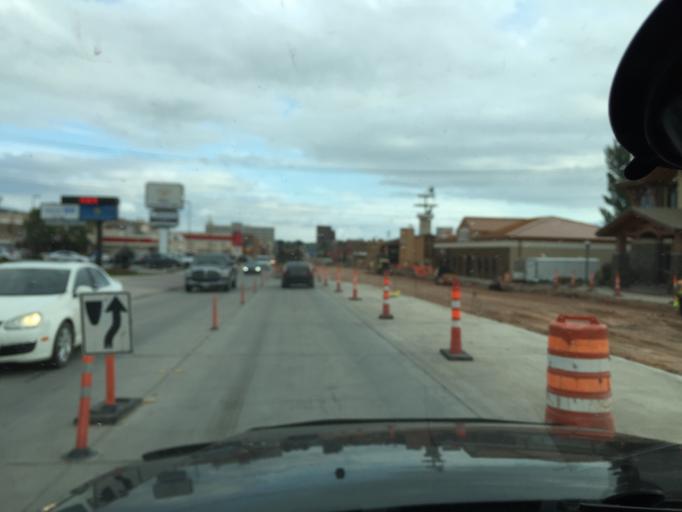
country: US
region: South Dakota
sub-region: Pennington County
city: Rapid City
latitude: 44.0775
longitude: -103.2321
